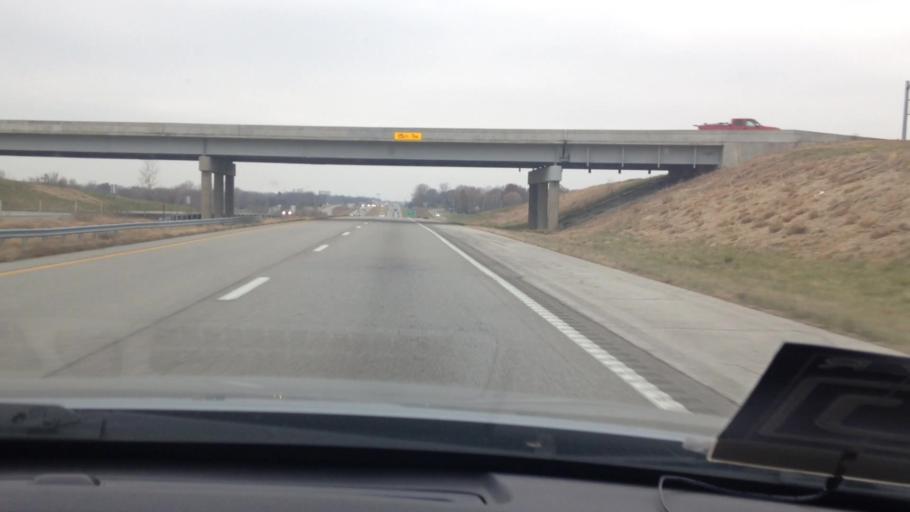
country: US
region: Missouri
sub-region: Cass County
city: Peculiar
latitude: 38.7226
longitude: -94.4544
